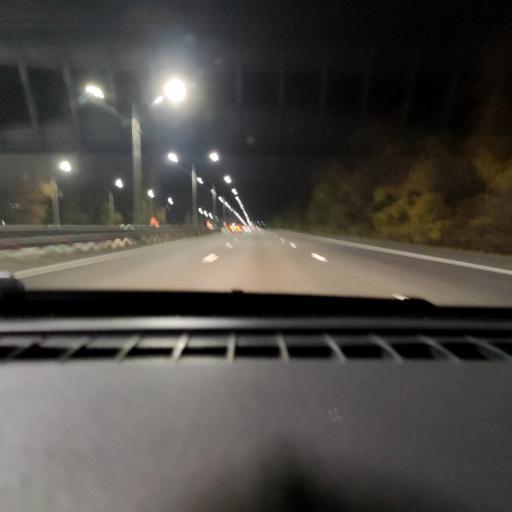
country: RU
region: Voronezj
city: Podgornoye
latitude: 51.8157
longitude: 39.2078
